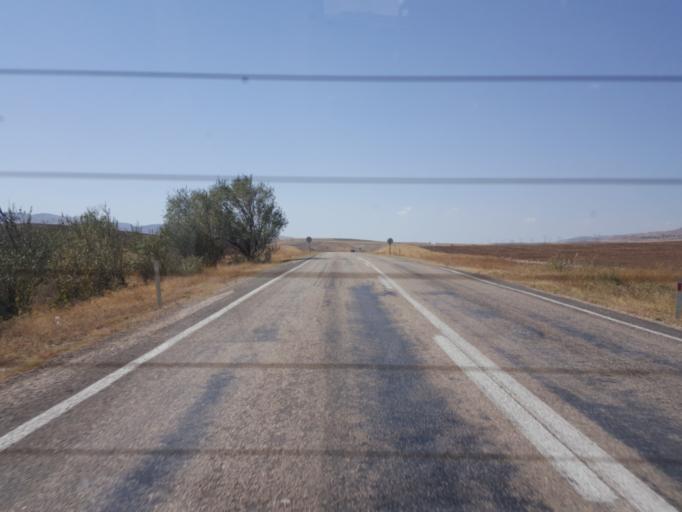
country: TR
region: Amasya
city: Dogantepe
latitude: 40.5750
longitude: 35.5925
